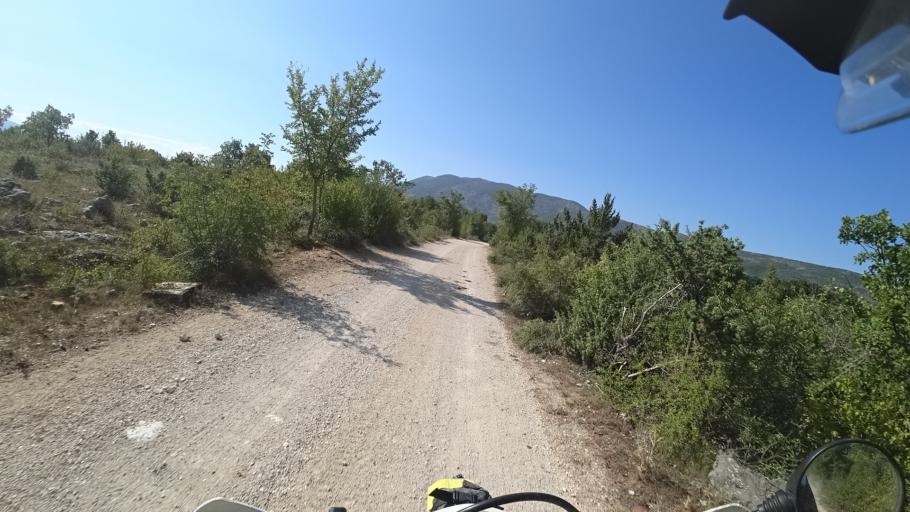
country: HR
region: Sibensko-Kniniska
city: Knin
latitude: 43.9717
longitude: 16.1844
